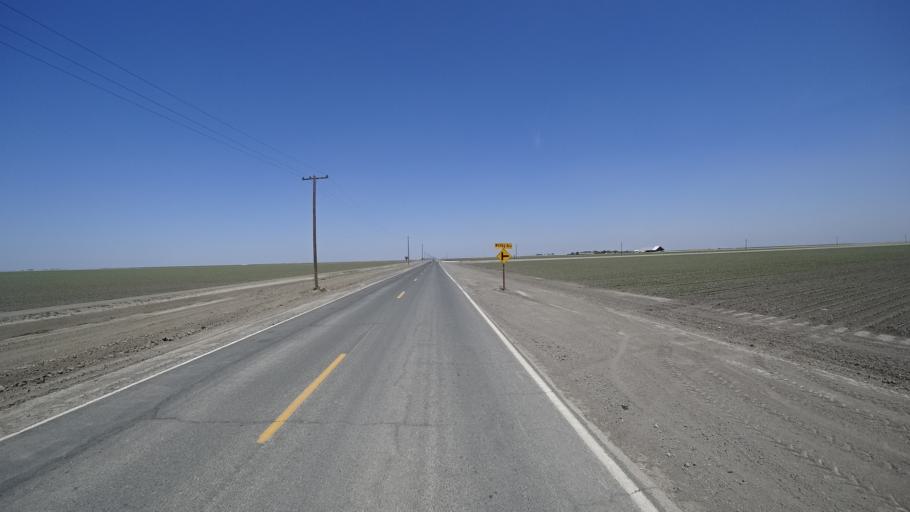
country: US
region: California
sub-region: Kings County
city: Corcoran
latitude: 36.0956
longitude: -119.6442
